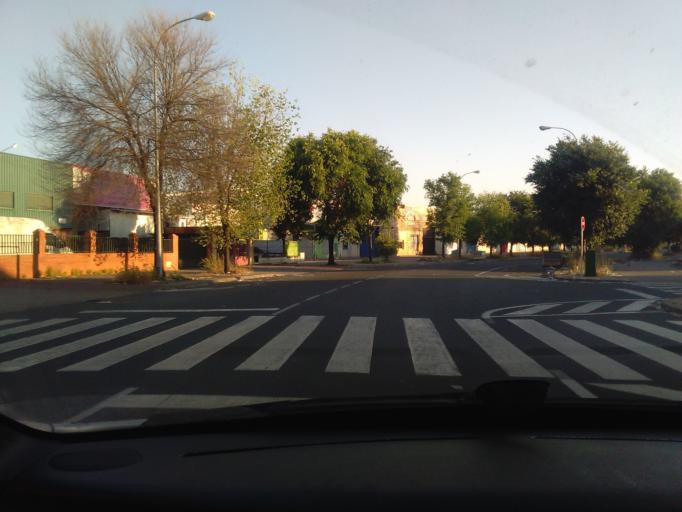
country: ES
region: Andalusia
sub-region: Provincia de Sevilla
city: Sevilla
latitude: 37.3938
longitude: -5.9393
